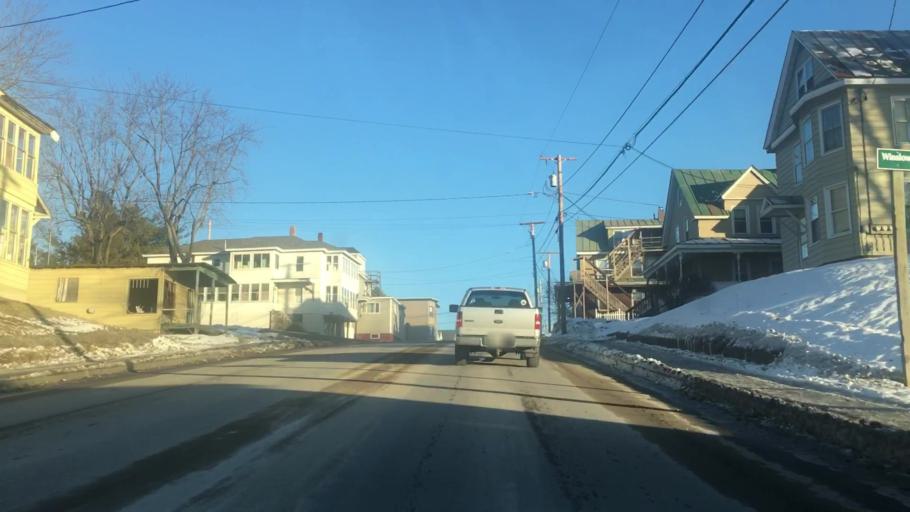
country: US
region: Maine
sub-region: Kennebec County
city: Winslow
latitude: 44.5472
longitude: -69.6246
